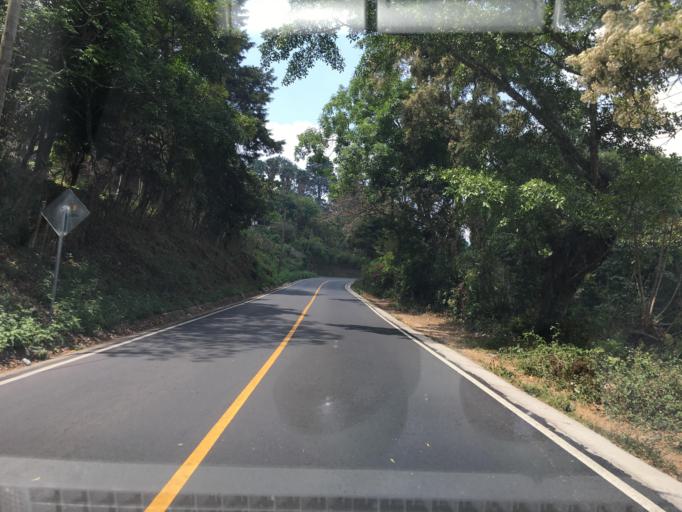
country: GT
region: Guatemala
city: Villa Canales
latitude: 14.4149
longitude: -90.5312
